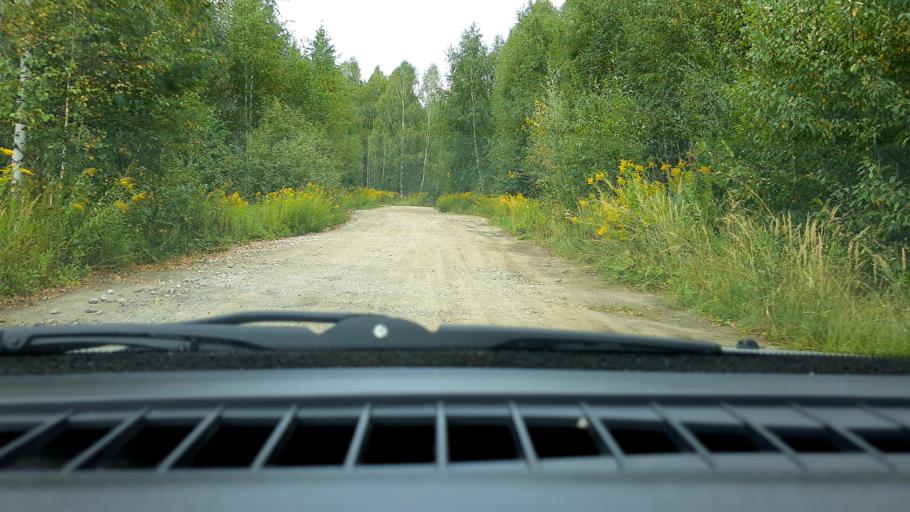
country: RU
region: Nizjnij Novgorod
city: Gorbatovka
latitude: 56.3111
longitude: 43.6898
